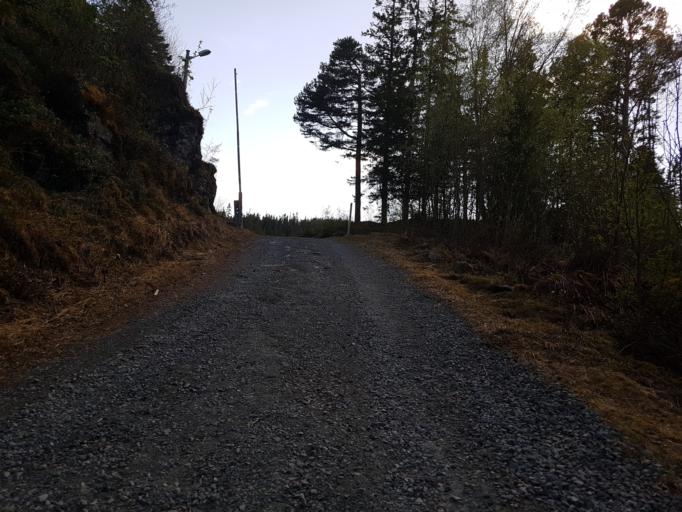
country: NO
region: Sor-Trondelag
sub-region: Trondheim
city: Trondheim
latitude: 63.4508
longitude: 10.2950
